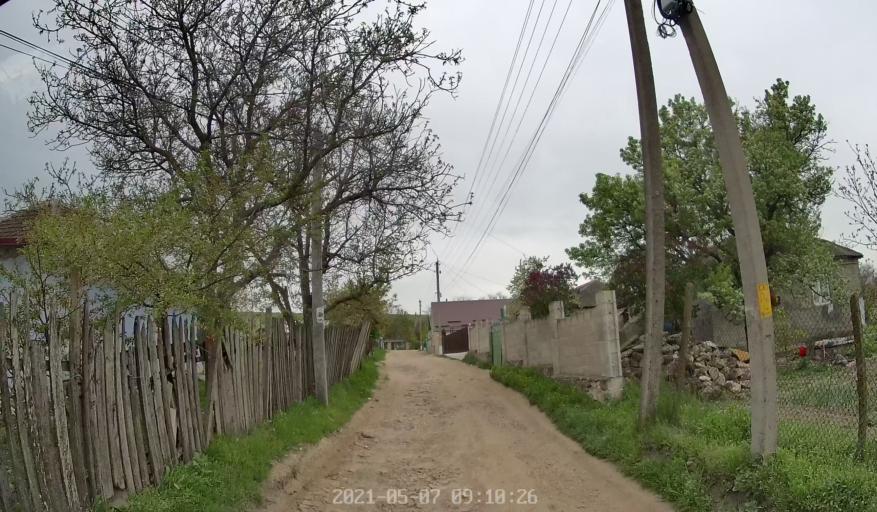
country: MD
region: Chisinau
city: Vadul lui Voda
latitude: 47.1175
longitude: 29.0073
